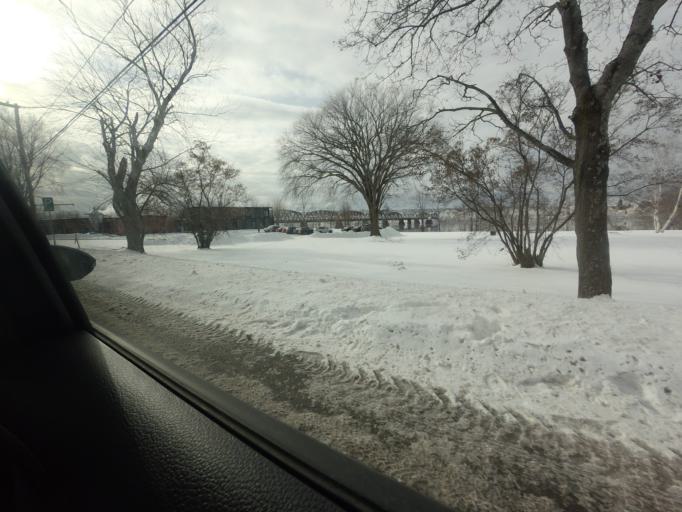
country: CA
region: New Brunswick
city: Fredericton
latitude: 45.9598
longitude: -66.6244
